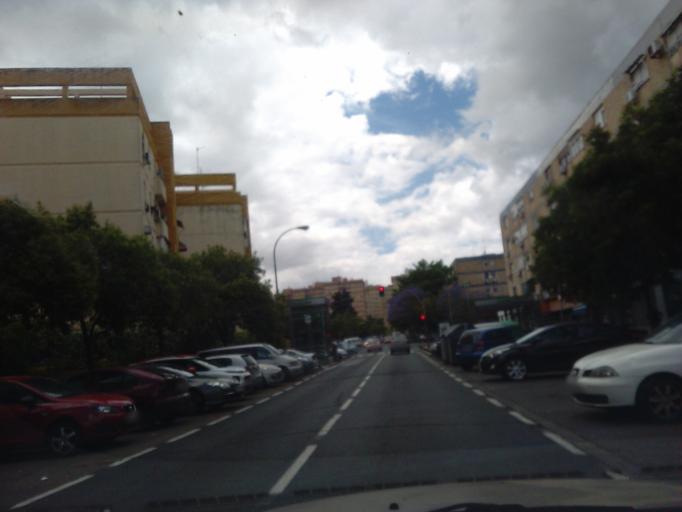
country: ES
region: Andalusia
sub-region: Provincia de Sevilla
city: Sevilla
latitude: 37.3764
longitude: -5.9525
